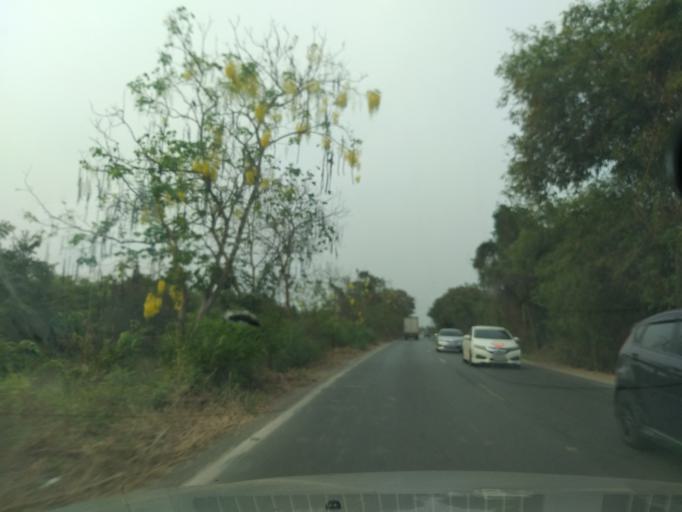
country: TH
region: Bangkok
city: Nong Chok
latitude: 13.9477
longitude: 100.8948
